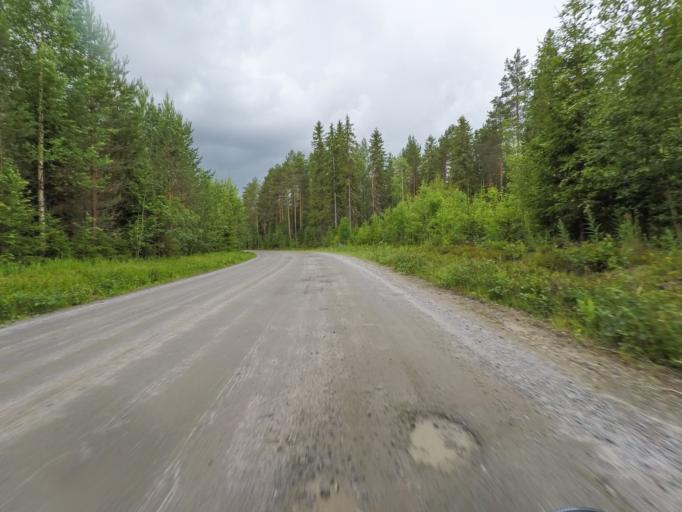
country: FI
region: Central Finland
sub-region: Jyvaeskylae
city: Hankasalmi
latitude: 62.4113
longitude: 26.6110
